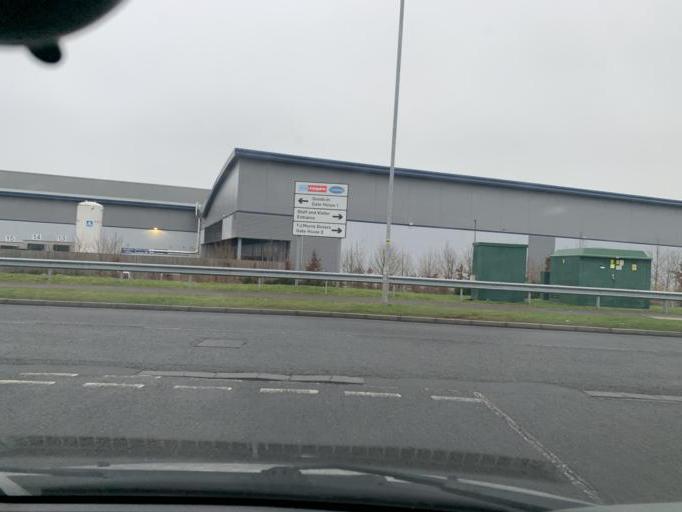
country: GB
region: England
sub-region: Wiltshire
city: Bulford
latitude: 51.1741
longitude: -1.7563
